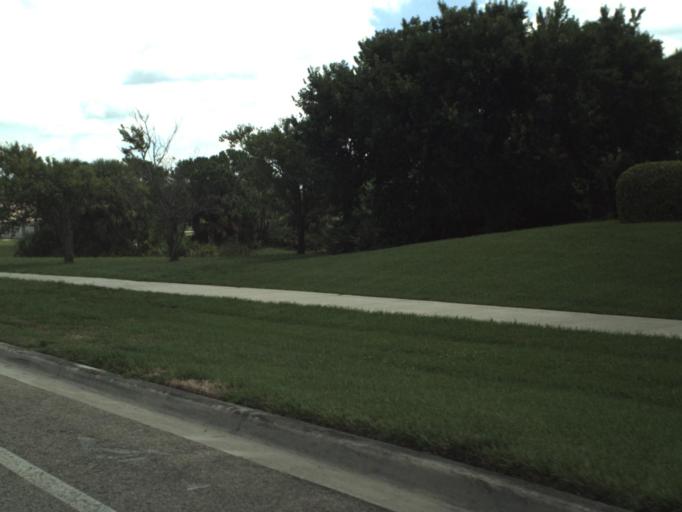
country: US
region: Florida
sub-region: Palm Beach County
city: North Palm Beach
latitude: 26.8515
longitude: -80.0962
